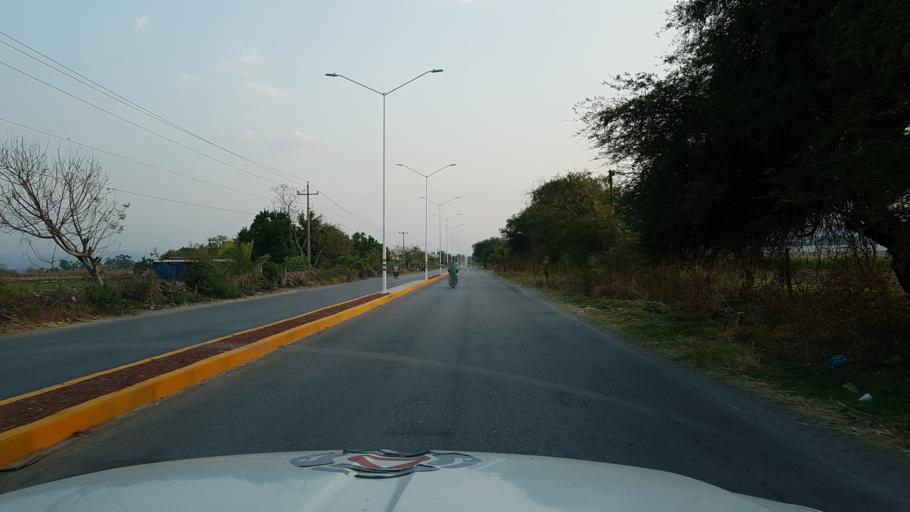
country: MX
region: Morelos
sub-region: Ayala
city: Abelardo L. Rodriguez
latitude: 18.7353
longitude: -98.9882
